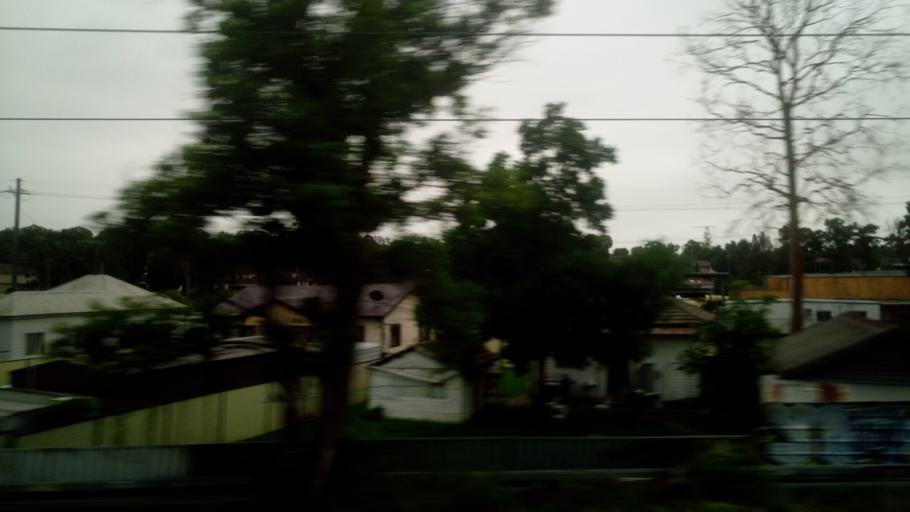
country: AU
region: New South Wales
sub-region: Blacktown
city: Blacktown
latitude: -33.7741
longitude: 150.9330
